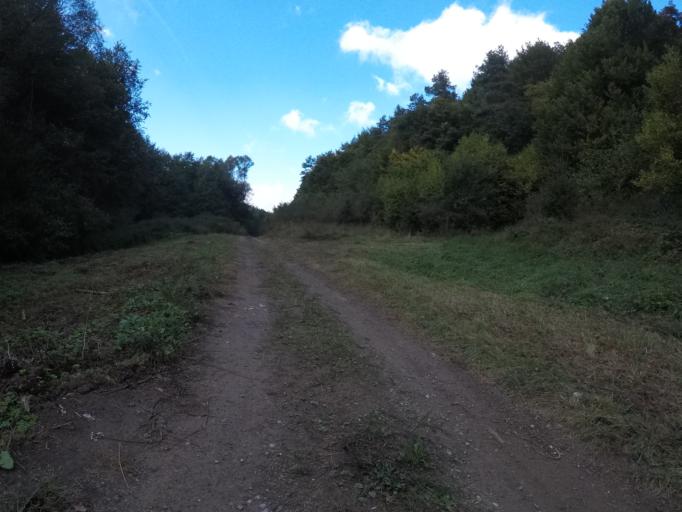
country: SK
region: Presovsky
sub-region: Okres Presov
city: Presov
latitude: 48.9304
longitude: 21.1694
